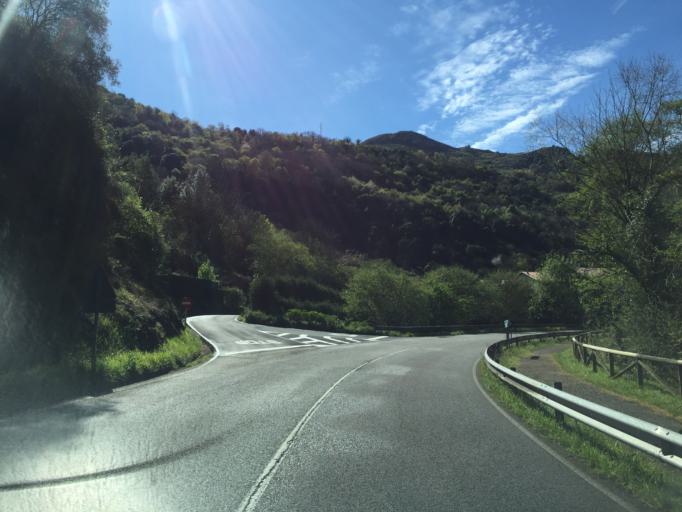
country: ES
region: Asturias
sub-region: Province of Asturias
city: Proaza
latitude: 43.2931
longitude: -5.9820
